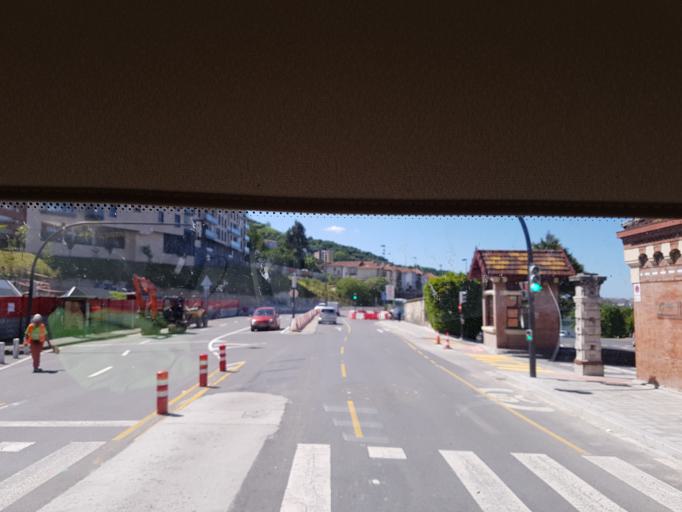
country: ES
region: Basque Country
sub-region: Bizkaia
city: Bilbao
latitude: 43.2603
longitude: -2.9540
